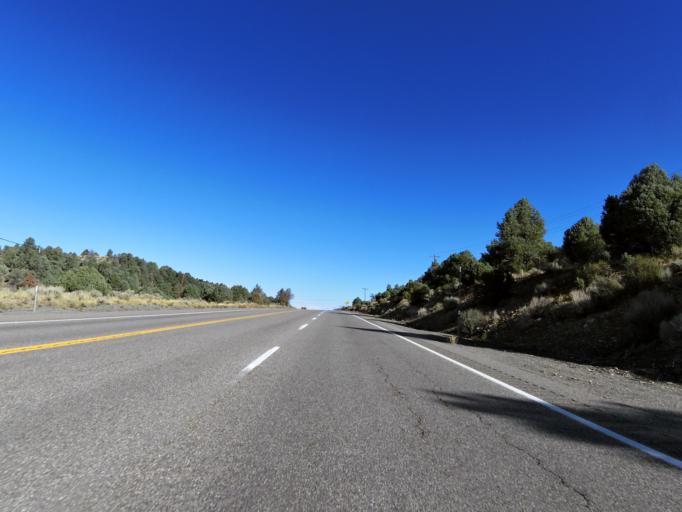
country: US
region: Nevada
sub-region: Douglas County
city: Gardnerville Ranchos
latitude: 38.7649
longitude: -119.5779
